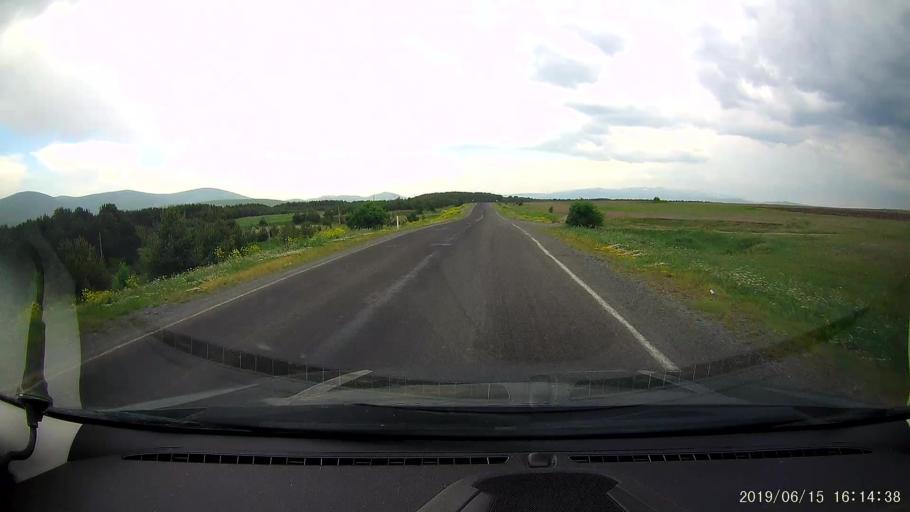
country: TR
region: Ardahan
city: Hanak
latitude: 41.2771
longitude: 42.8463
